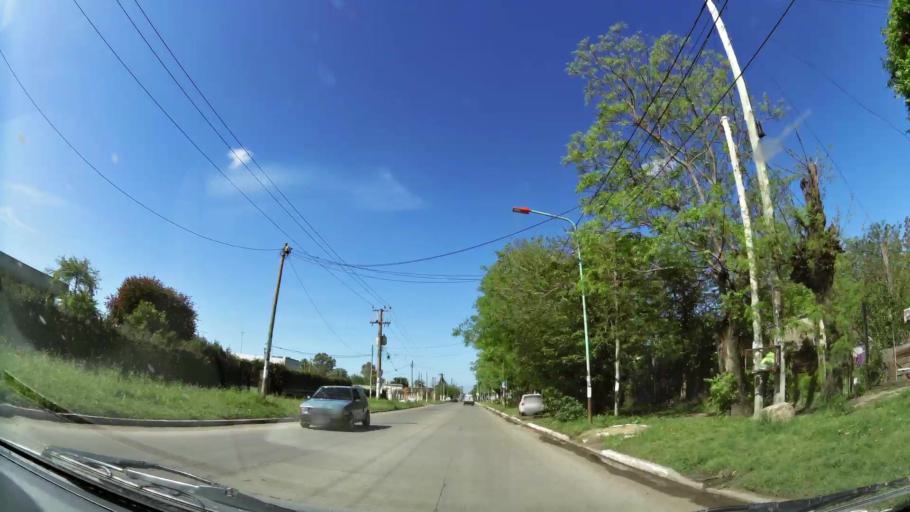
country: AR
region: Buenos Aires
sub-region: Partido de Quilmes
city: Quilmes
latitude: -34.7973
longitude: -58.2585
